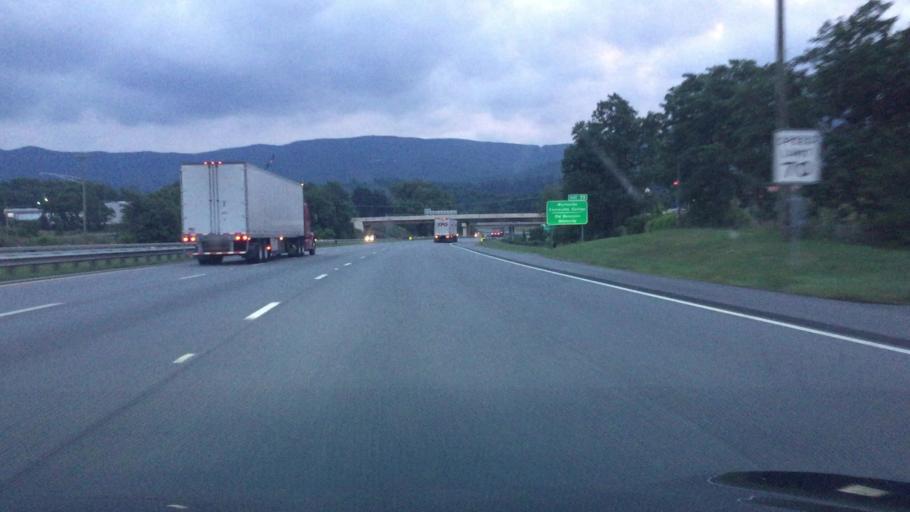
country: US
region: Virginia
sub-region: Wythe County
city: Wytheville
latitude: 36.9547
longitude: -81.0556
